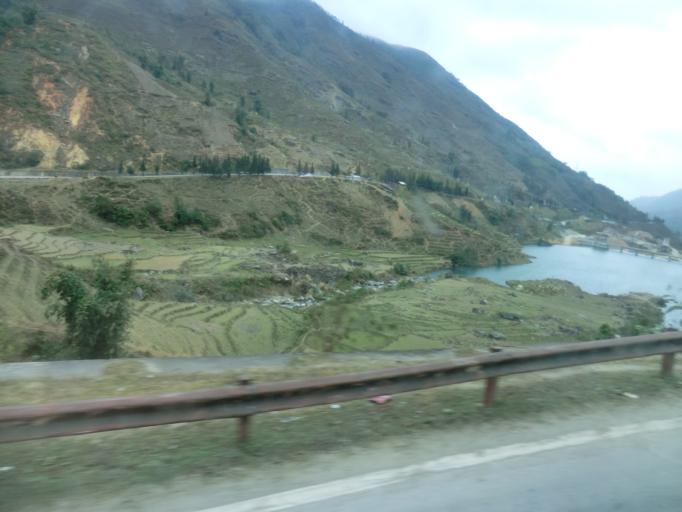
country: VN
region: Lao Cai
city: Sa Pa
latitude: 22.4112
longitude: 103.9002
